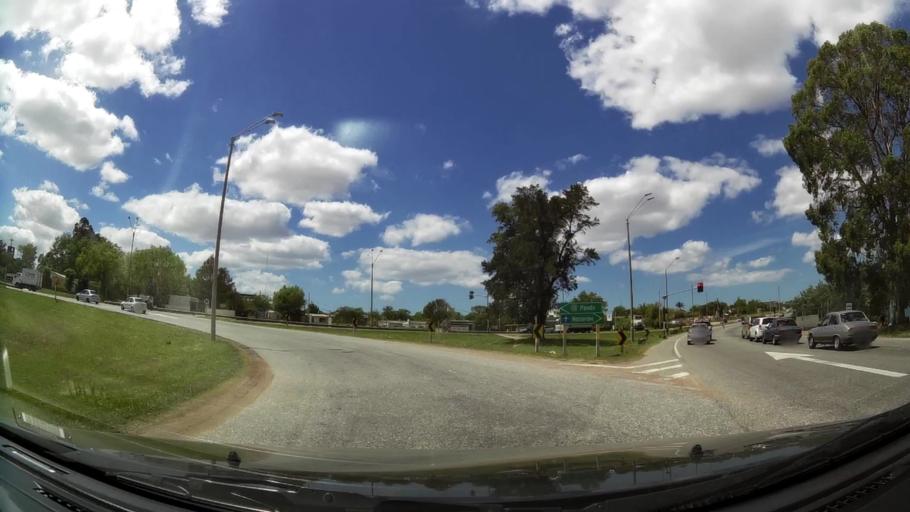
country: UY
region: Canelones
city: Colonia Nicolich
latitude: -34.8204
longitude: -56.0092
